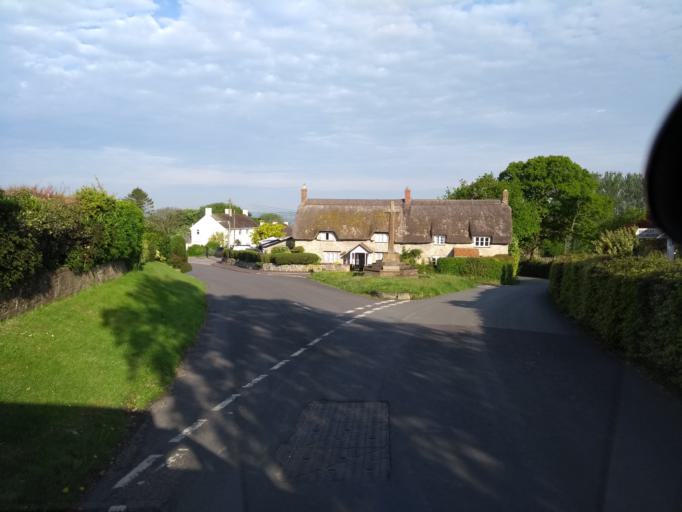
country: GB
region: England
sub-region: Devon
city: Axminster
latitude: 50.8004
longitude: -2.9350
